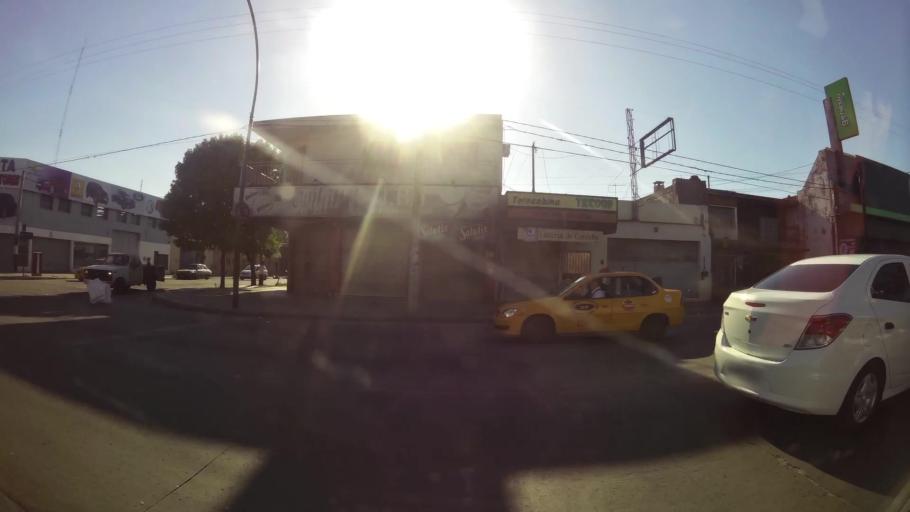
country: AR
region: Cordoba
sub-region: Departamento de Capital
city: Cordoba
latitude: -31.3815
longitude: -64.1760
